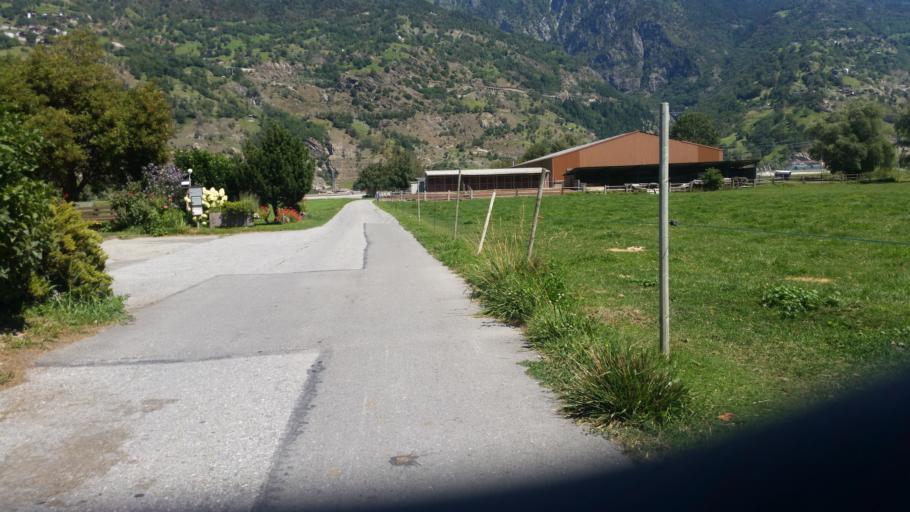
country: CH
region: Valais
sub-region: Visp District
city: Baltschieder
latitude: 46.3004
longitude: 7.8518
